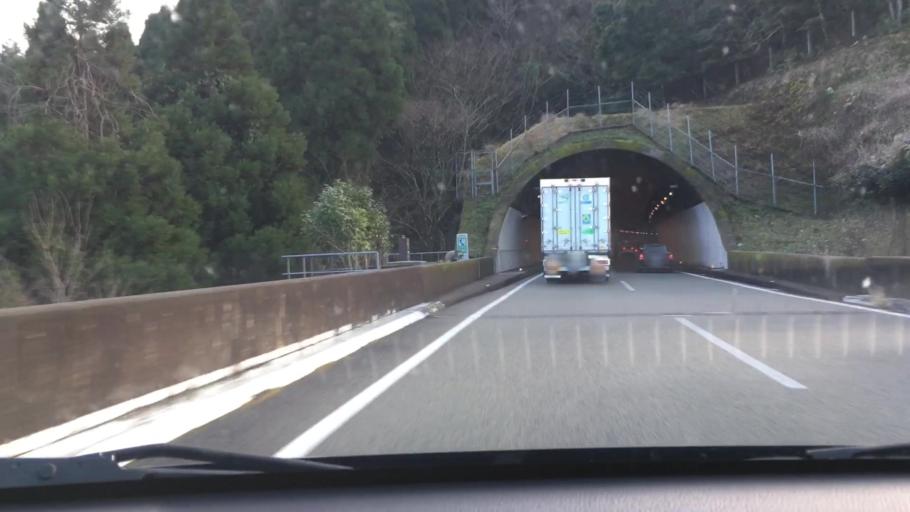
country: JP
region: Kumamoto
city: Hitoyoshi
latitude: 32.1343
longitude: 130.8041
